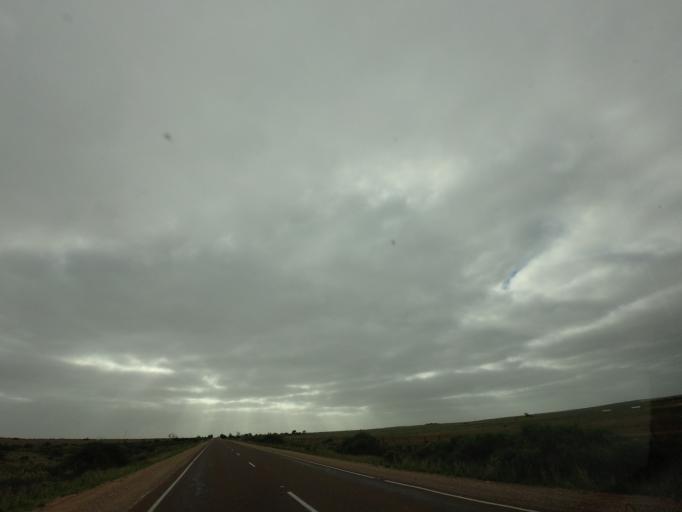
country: AU
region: South Australia
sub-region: Ceduna
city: Ceduna
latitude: -32.1245
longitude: 133.7124
